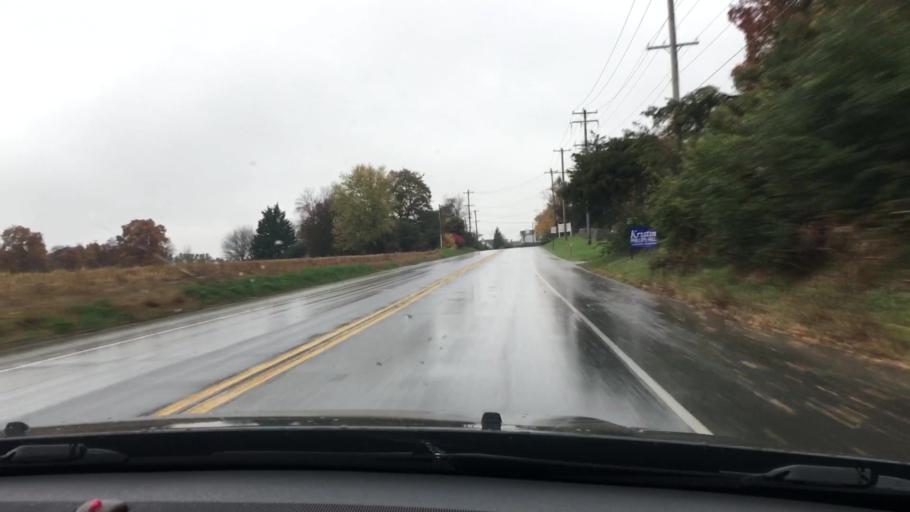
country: US
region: Pennsylvania
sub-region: York County
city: Susquehanna Trails
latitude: 39.8026
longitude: -76.3680
